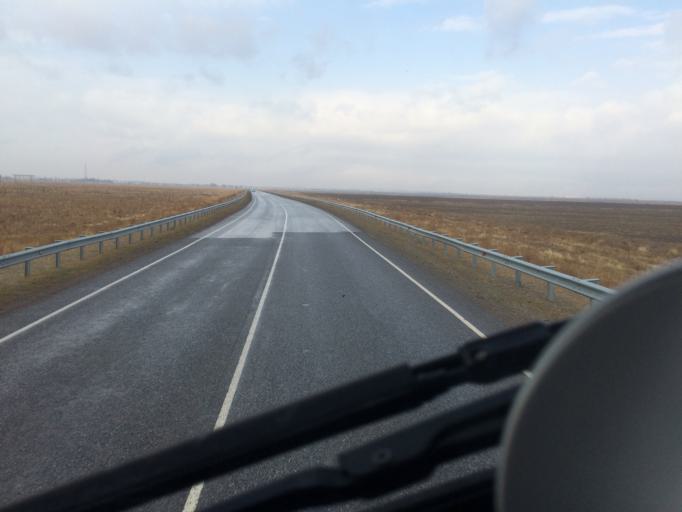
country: KZ
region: Zhambyl
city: Georgiyevka
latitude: 43.0733
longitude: 74.7343
